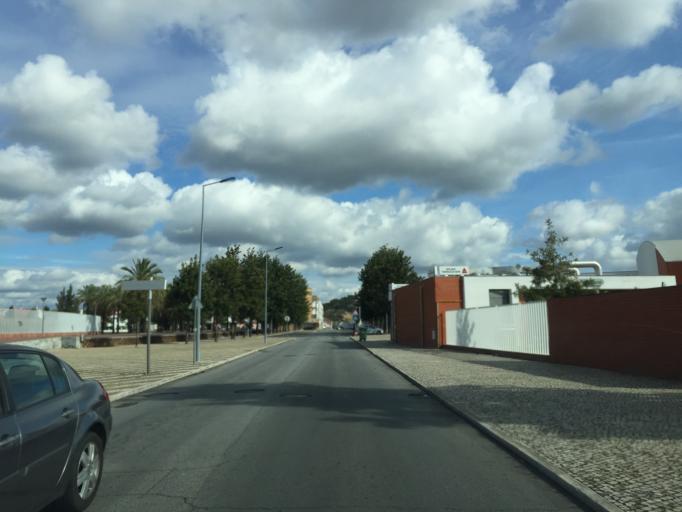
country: PT
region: Portalegre
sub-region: Ponte de Sor
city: Ponte de Sor
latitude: 39.2526
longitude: -8.0136
